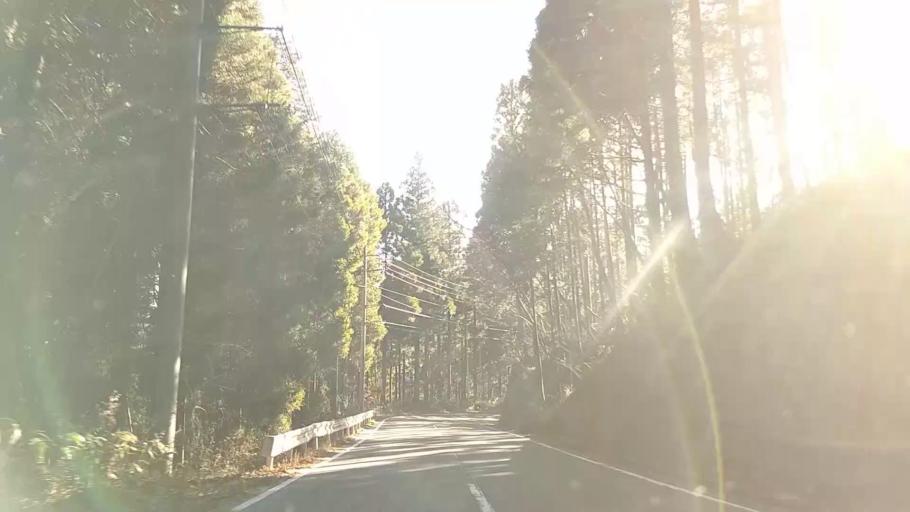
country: JP
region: Yamanashi
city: Otsuki
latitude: 35.5103
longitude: 138.9823
